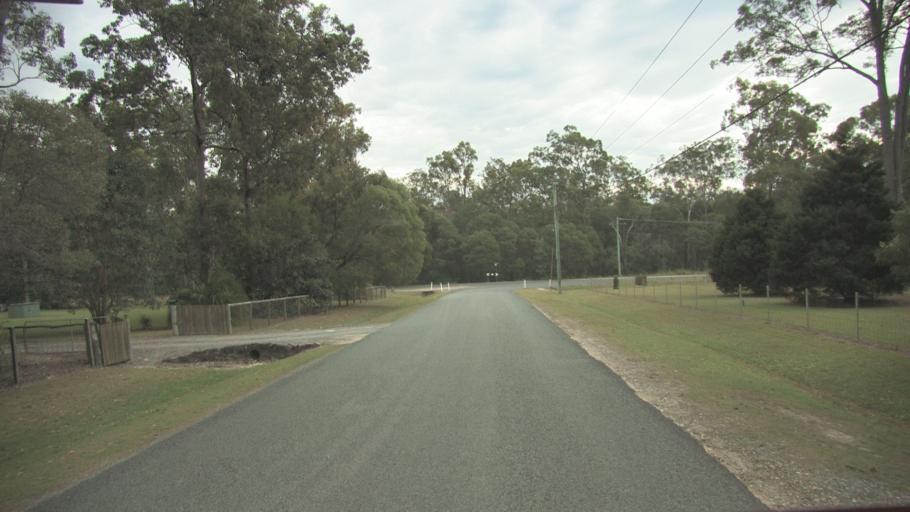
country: AU
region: Queensland
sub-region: Logan
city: Chambers Flat
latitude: -27.7869
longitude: 153.1091
